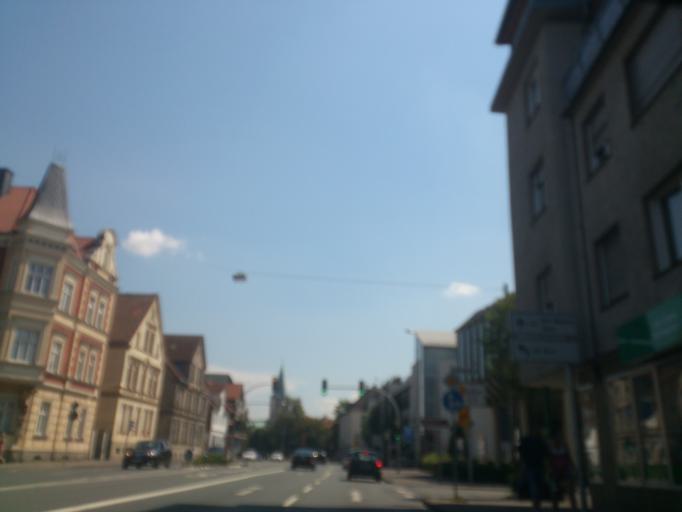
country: DE
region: North Rhine-Westphalia
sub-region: Regierungsbezirk Detmold
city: Paderborn
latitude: 51.7215
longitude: 8.7462
